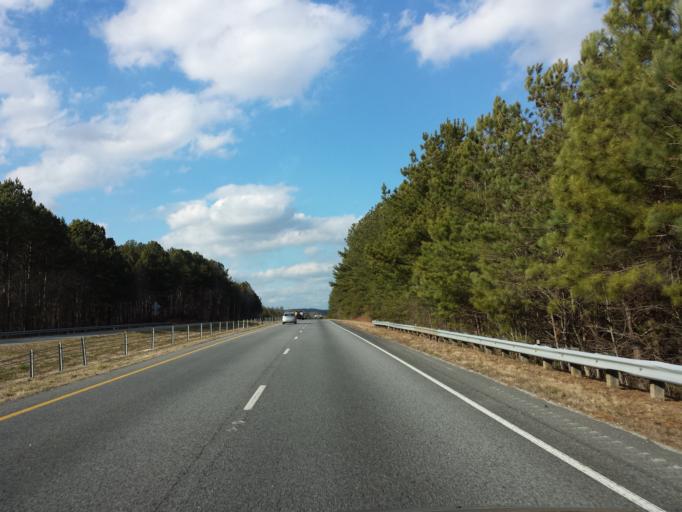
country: US
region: Georgia
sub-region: Lumpkin County
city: Dahlonega
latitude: 34.4289
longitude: -83.9914
